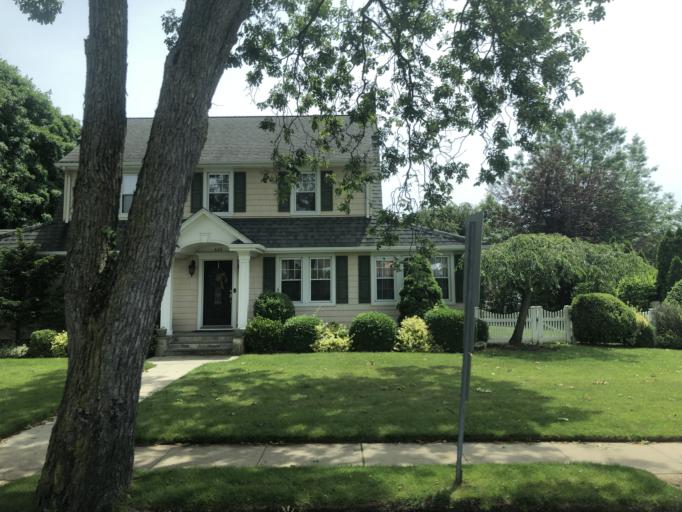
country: US
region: New York
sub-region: Nassau County
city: Rockville Centre
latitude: 40.6727
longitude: -73.6366
